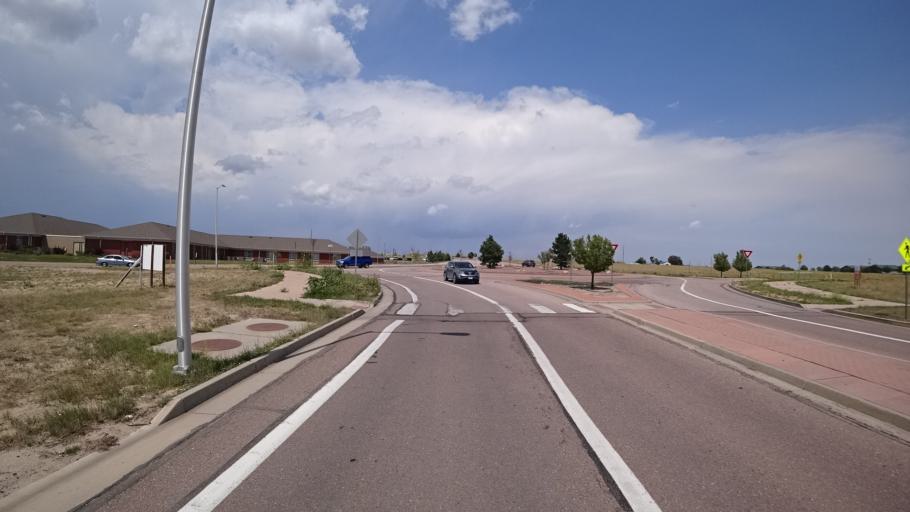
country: US
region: Colorado
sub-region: El Paso County
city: Black Forest
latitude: 38.9365
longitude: -104.7119
